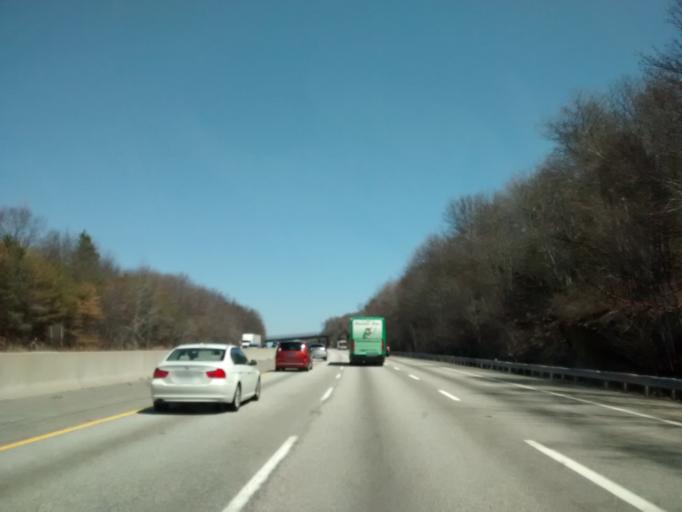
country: US
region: Massachusetts
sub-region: Worcester County
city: Westborough
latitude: 42.2363
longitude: -71.6034
